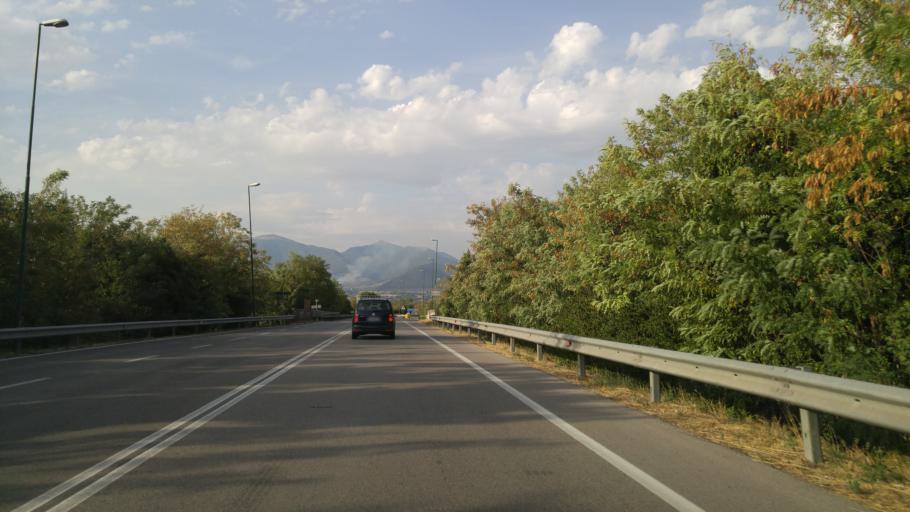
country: IT
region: Umbria
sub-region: Provincia di Perugia
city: Spoleto
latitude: 42.7448
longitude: 12.7435
